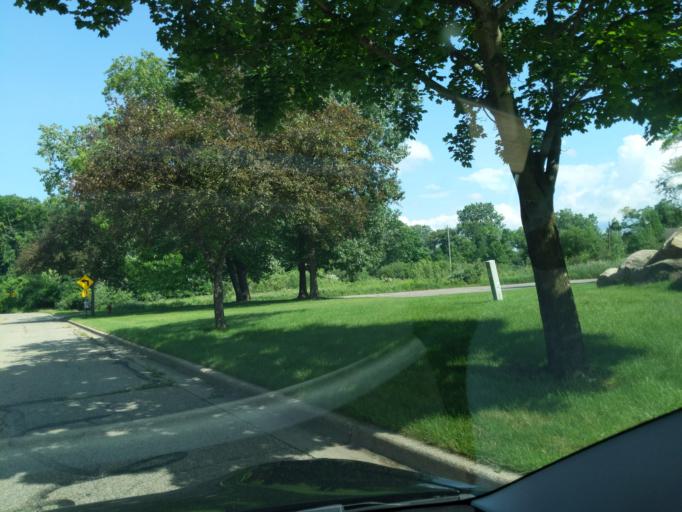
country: US
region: Michigan
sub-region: Jackson County
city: Jackson
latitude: 42.2293
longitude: -84.3679
